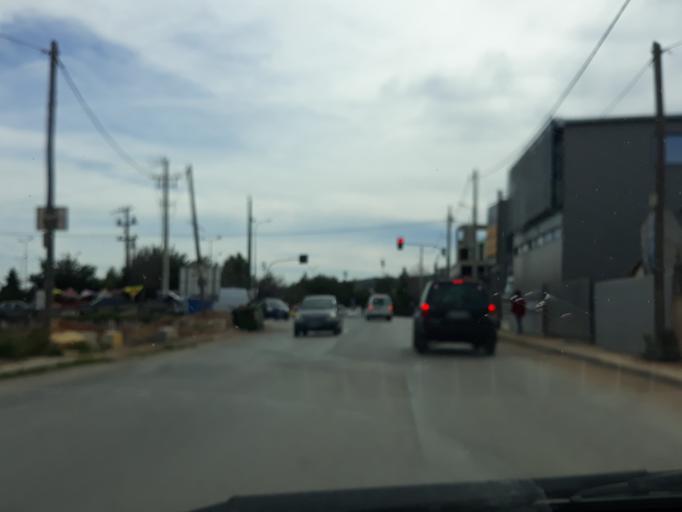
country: GR
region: Attica
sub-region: Nomarchia Dytikis Attikis
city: Ano Liosia
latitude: 38.0803
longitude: 23.7101
